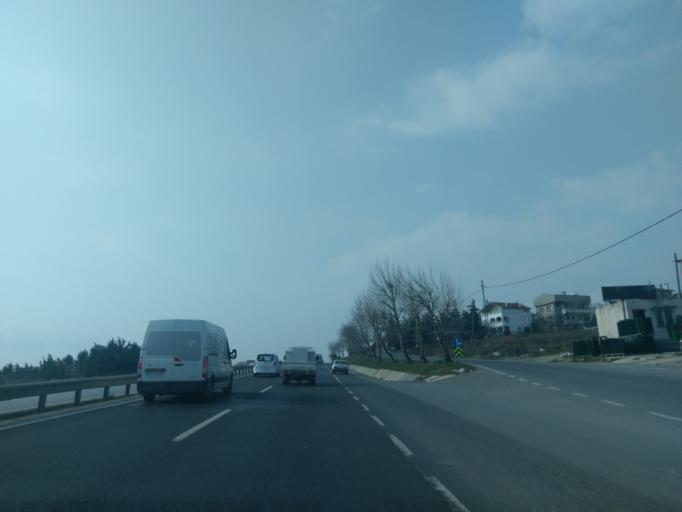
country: TR
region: Istanbul
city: Kumburgaz
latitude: 41.0116
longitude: 28.4981
